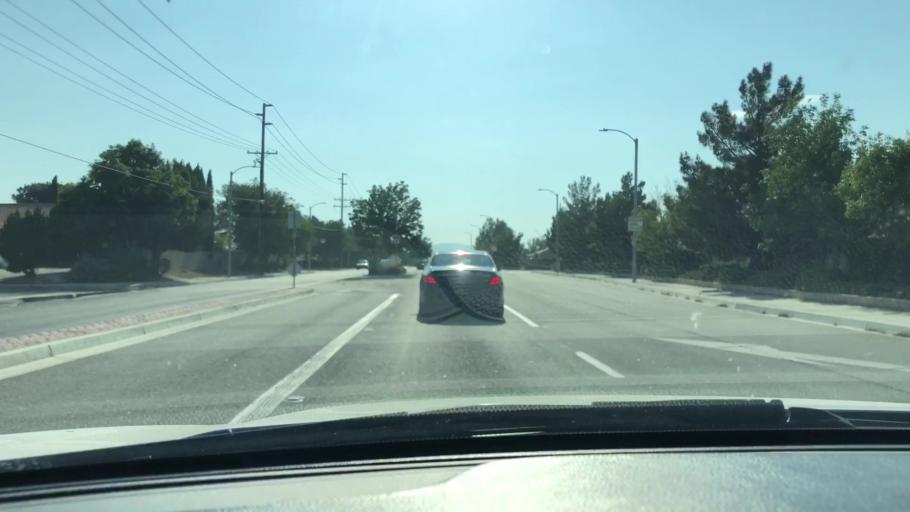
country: US
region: California
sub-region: Los Angeles County
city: Quartz Hill
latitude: 34.6894
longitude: -118.1966
